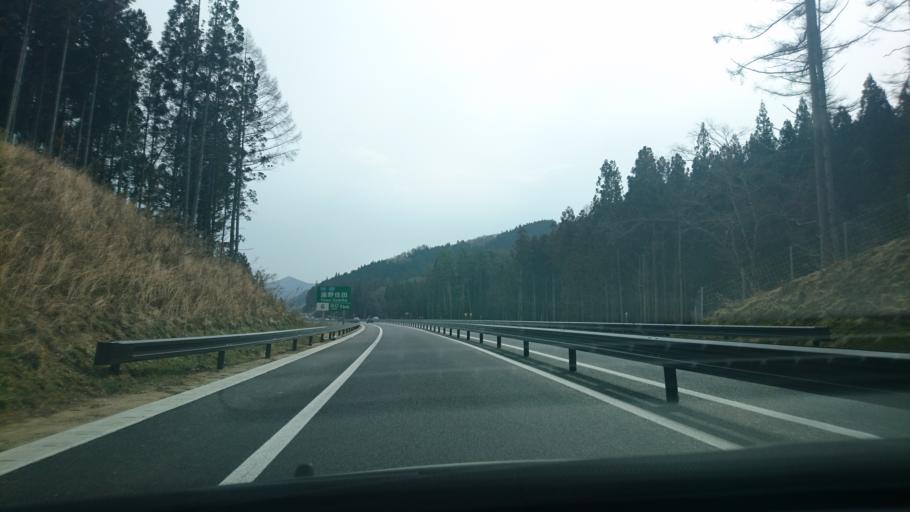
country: JP
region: Iwate
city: Tono
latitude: 39.2684
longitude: 141.5758
